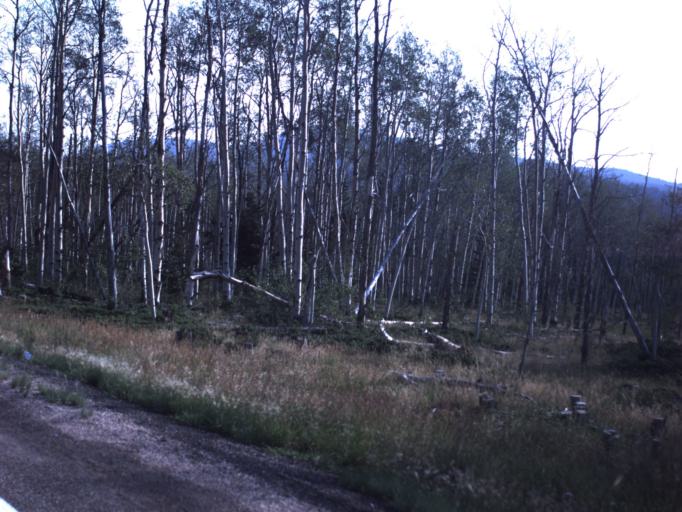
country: US
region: Utah
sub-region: Uintah County
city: Maeser
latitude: 40.7196
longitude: -109.4732
